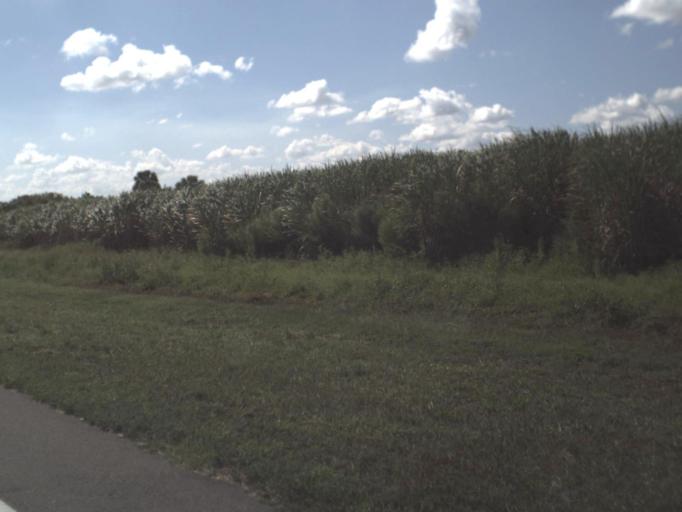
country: US
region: Florida
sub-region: Glades County
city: Moore Haven
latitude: 26.8280
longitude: -81.1886
